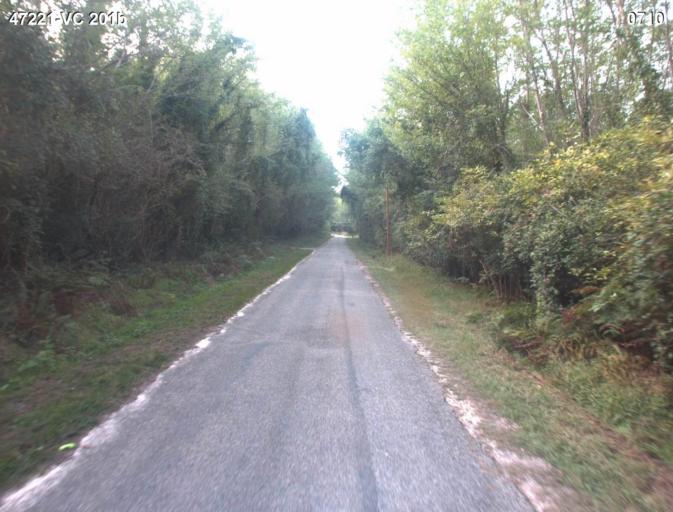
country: FR
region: Aquitaine
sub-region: Departement du Lot-et-Garonne
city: Mezin
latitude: 44.0801
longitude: 0.2410
